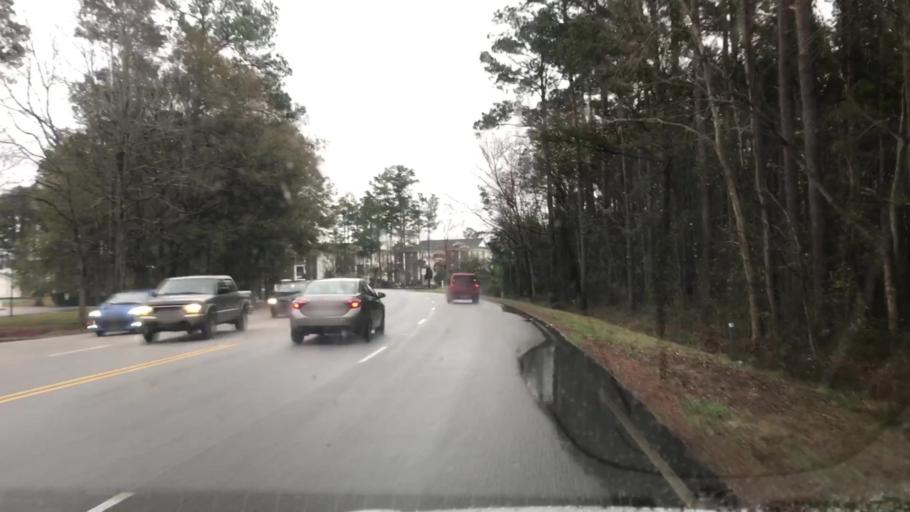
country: US
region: South Carolina
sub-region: Horry County
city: Forestbrook
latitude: 33.7213
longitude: -78.9247
